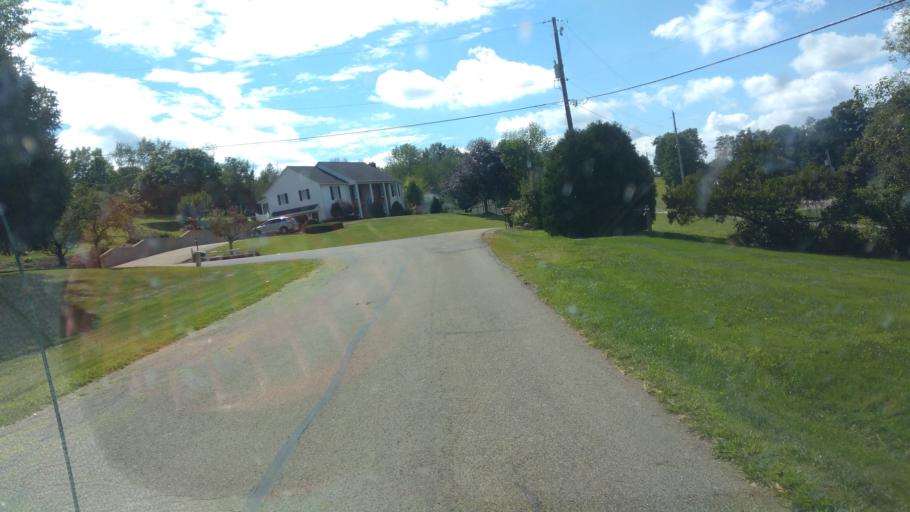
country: US
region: Ohio
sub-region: Holmes County
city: Millersburg
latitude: 40.5610
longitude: -81.8080
